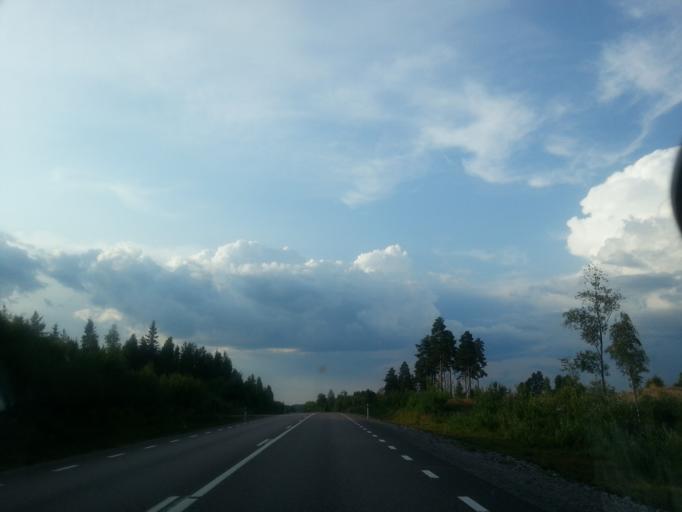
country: SE
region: Dalarna
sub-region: Avesta Kommun
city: Horndal
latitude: 60.3267
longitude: 16.4142
